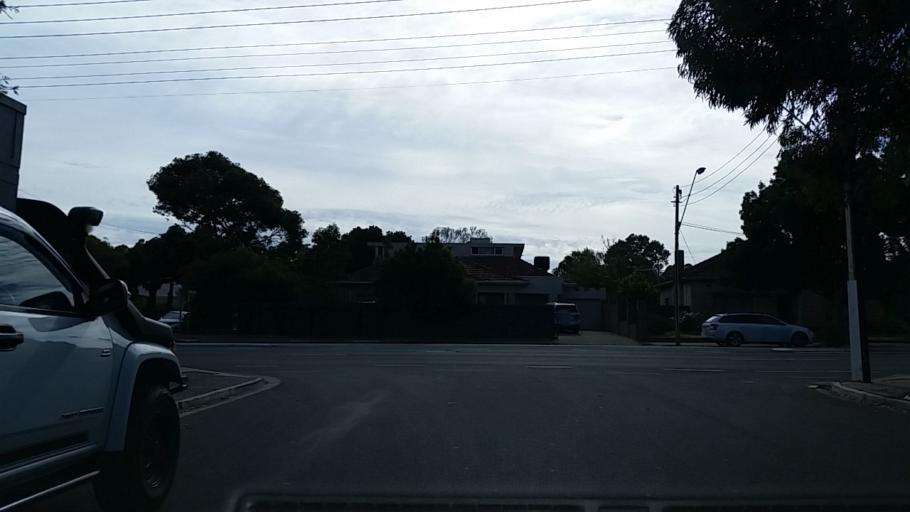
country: AU
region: South Australia
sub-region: Campbelltown
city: Hectorville
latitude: -34.9083
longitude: 138.6575
